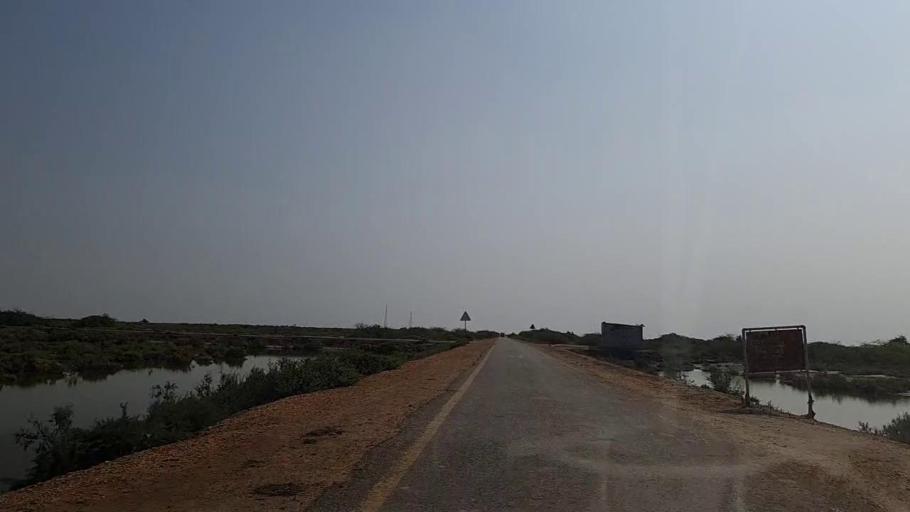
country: PK
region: Sindh
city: Chuhar Jamali
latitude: 24.1759
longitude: 67.8901
